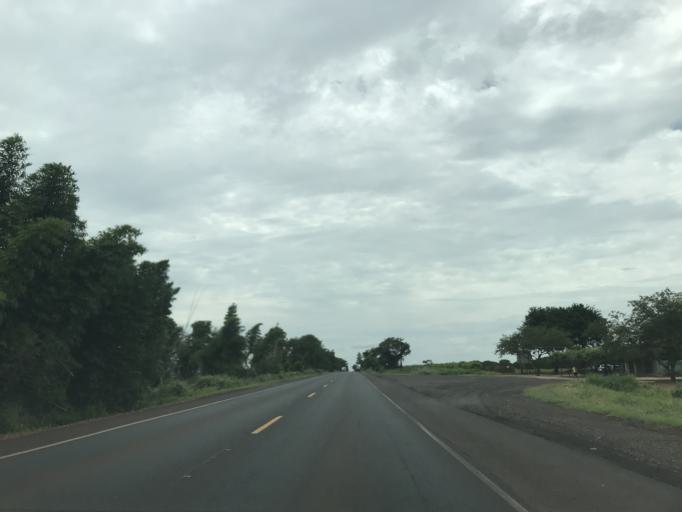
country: BR
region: Minas Gerais
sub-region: Frutal
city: Frutal
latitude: -20.0860
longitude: -49.0812
